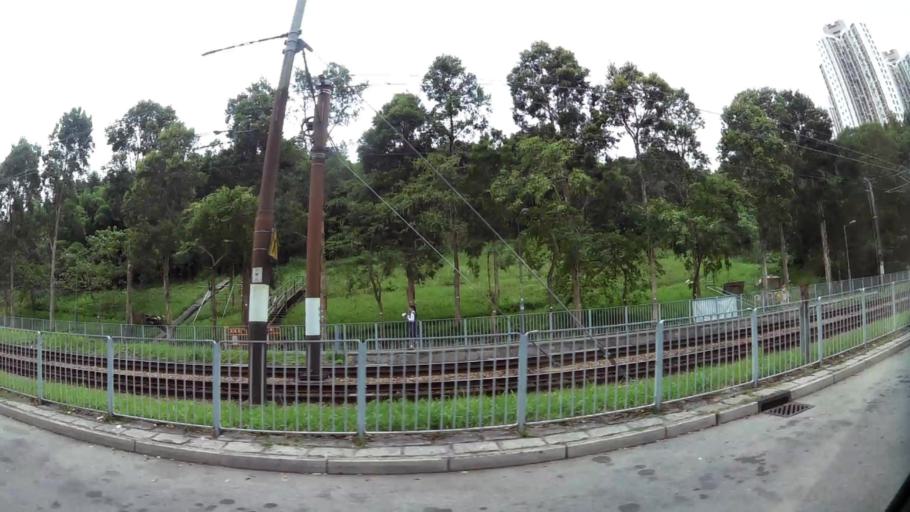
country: HK
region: Tuen Mun
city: Tuen Mun
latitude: 22.4050
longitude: 113.9654
